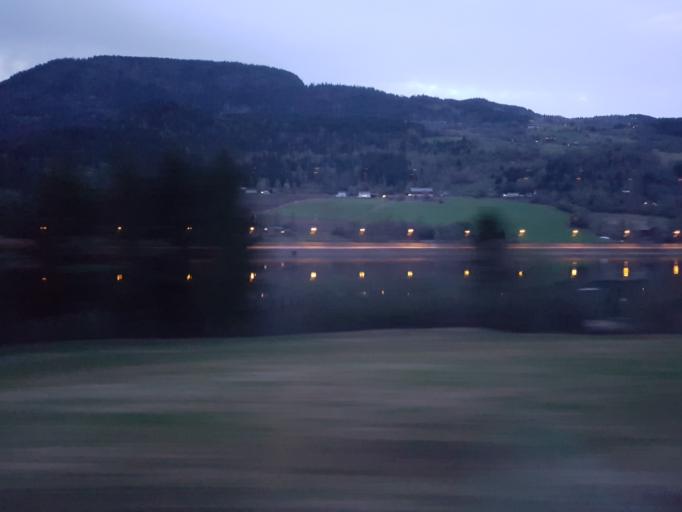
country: NO
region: Oppland
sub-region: Oyer
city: Tretten
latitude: 61.2753
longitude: 10.3672
